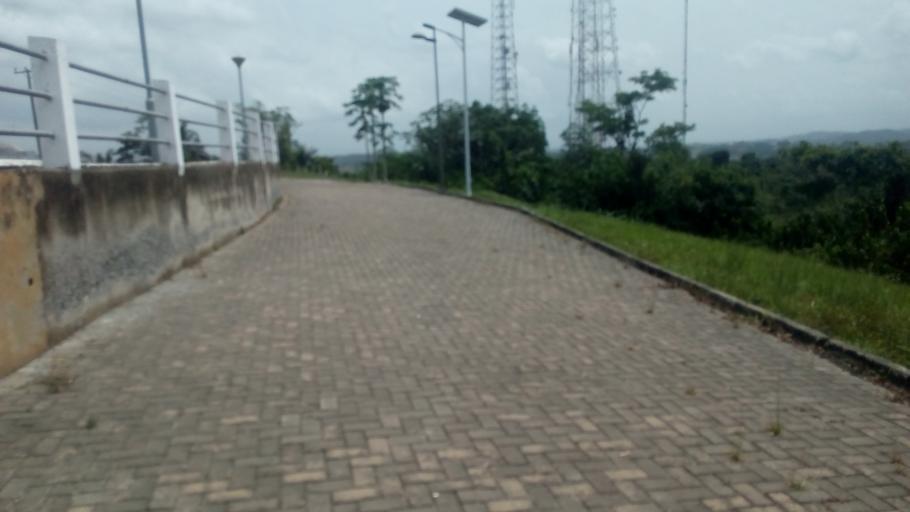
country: GH
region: Western
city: Tarkwa
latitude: 5.3009
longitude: -2.0100
